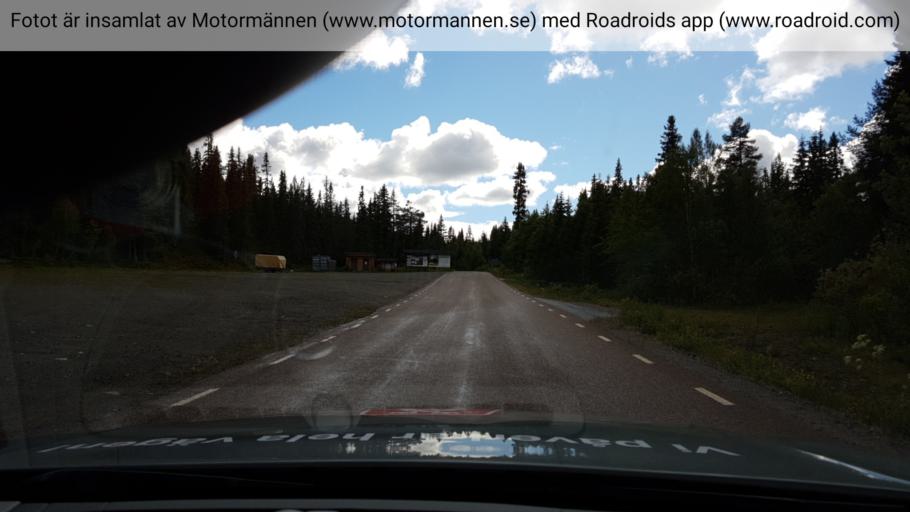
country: SE
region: Jaemtland
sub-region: Are Kommun
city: Jarpen
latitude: 63.0777
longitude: 13.7449
